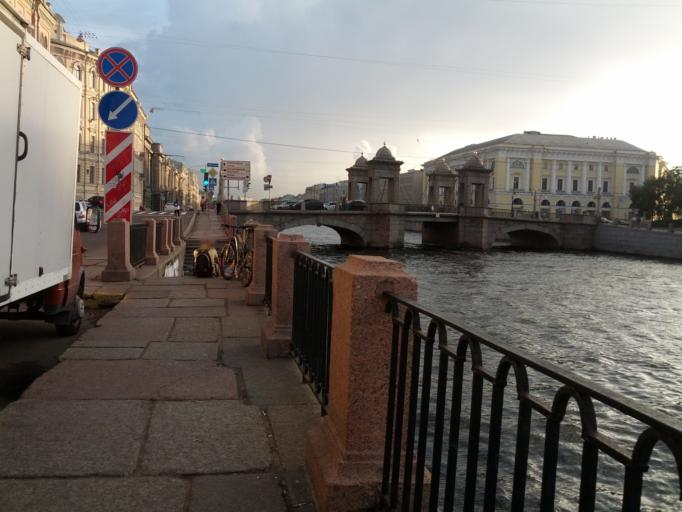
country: RU
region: St.-Petersburg
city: Centralniy
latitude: 59.9288
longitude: 30.3374
